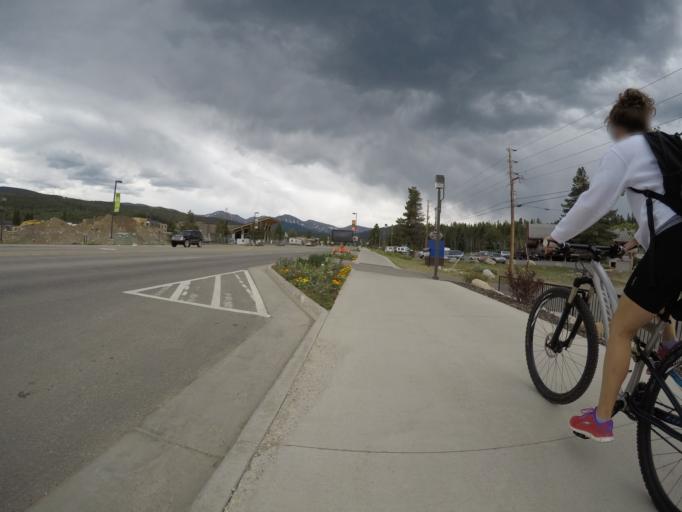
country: US
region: Colorado
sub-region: Grand County
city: Fraser
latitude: 39.9266
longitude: -105.7882
